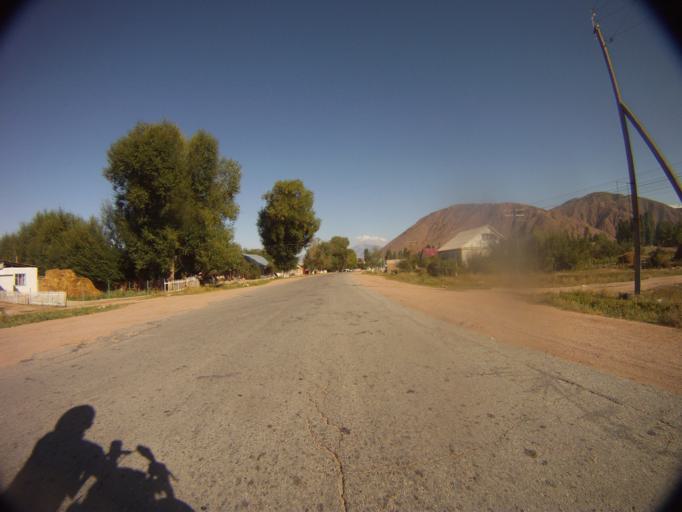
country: KG
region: Ysyk-Koel
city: Bokombayevskoye
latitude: 42.1371
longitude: 76.8290
